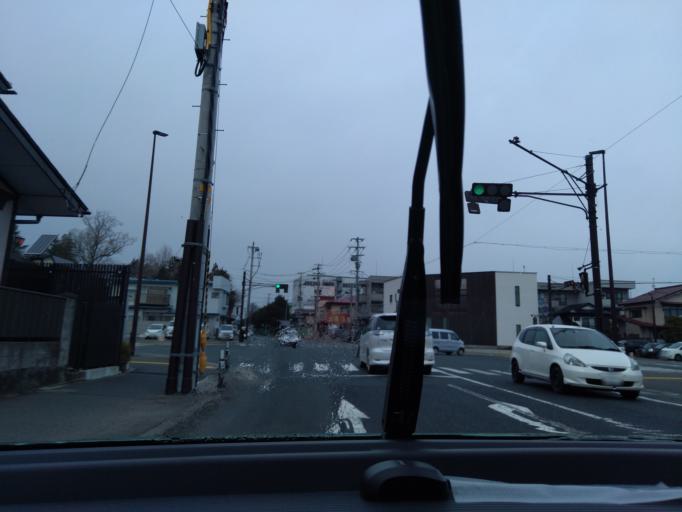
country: JP
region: Iwate
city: Morioka-shi
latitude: 39.7114
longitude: 141.1419
